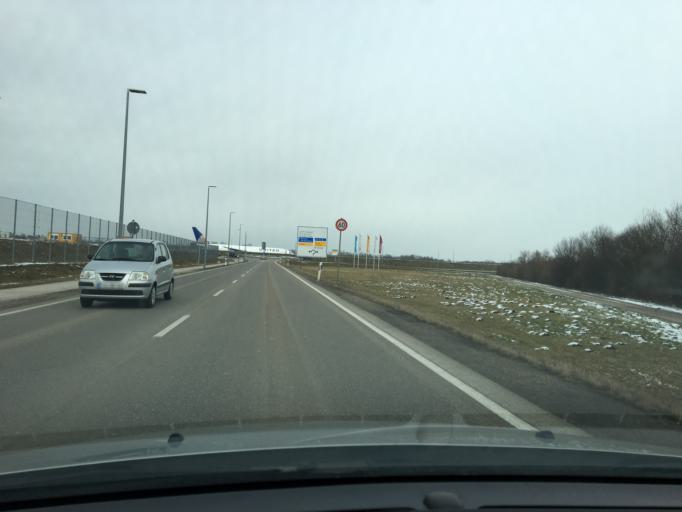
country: DE
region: Bavaria
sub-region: Upper Bavaria
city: Marzling
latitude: 48.3587
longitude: 11.8061
